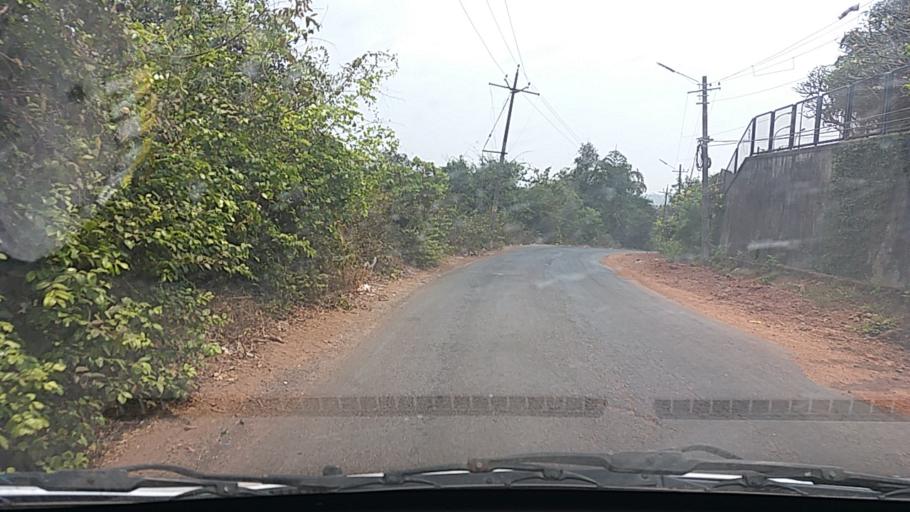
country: IN
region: Goa
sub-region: North Goa
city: Saligao
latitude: 15.5334
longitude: 73.7981
